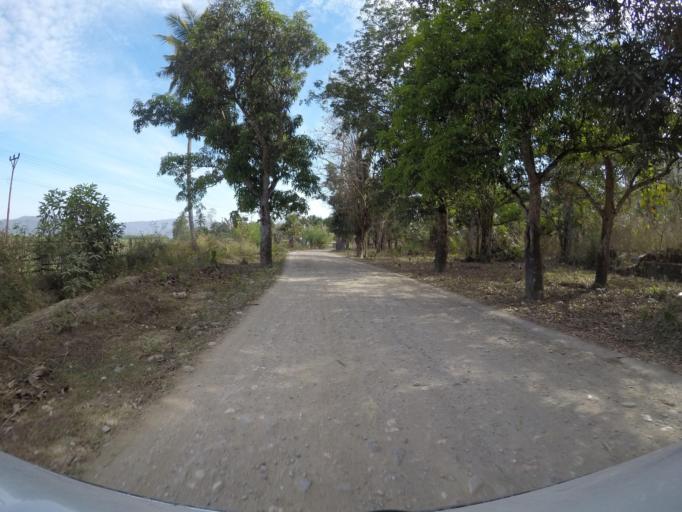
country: TL
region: Bobonaro
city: Maliana
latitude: -8.8855
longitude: 125.2088
